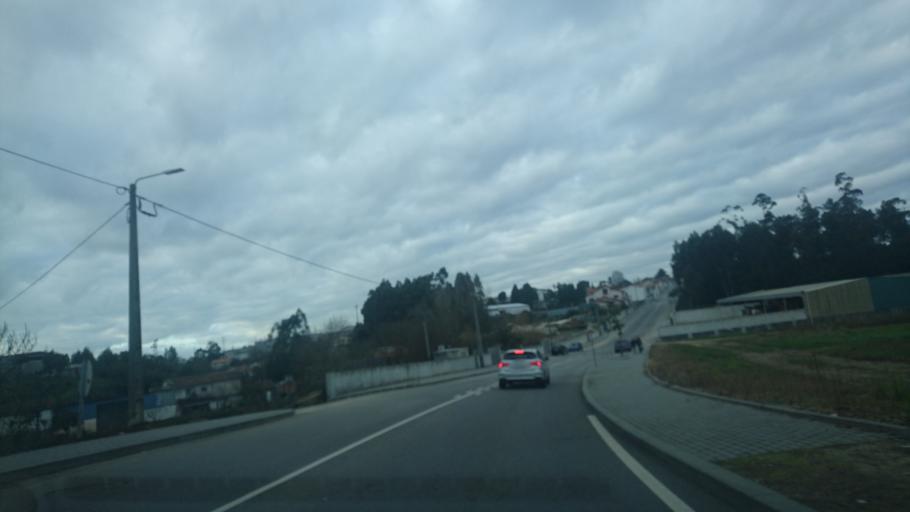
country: PT
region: Aveiro
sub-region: Santa Maria da Feira
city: Pacos de Brandao
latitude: 40.9639
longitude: -8.5917
